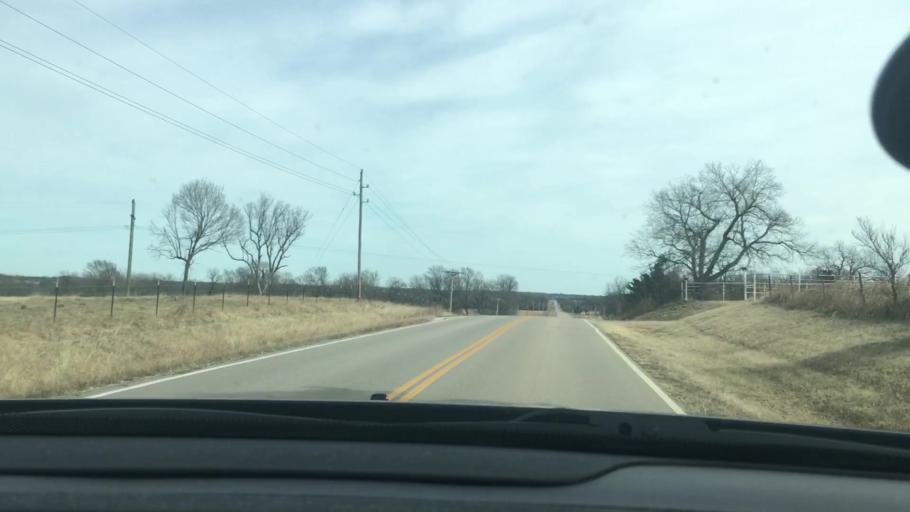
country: US
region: Oklahoma
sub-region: Murray County
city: Sulphur
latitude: 34.4050
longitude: -96.8797
